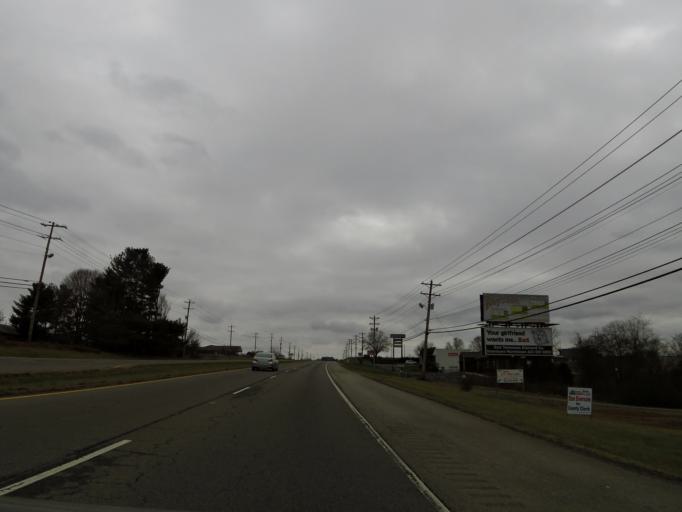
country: US
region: Tennessee
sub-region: Hamblen County
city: Morristown
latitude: 36.1894
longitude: -83.3672
